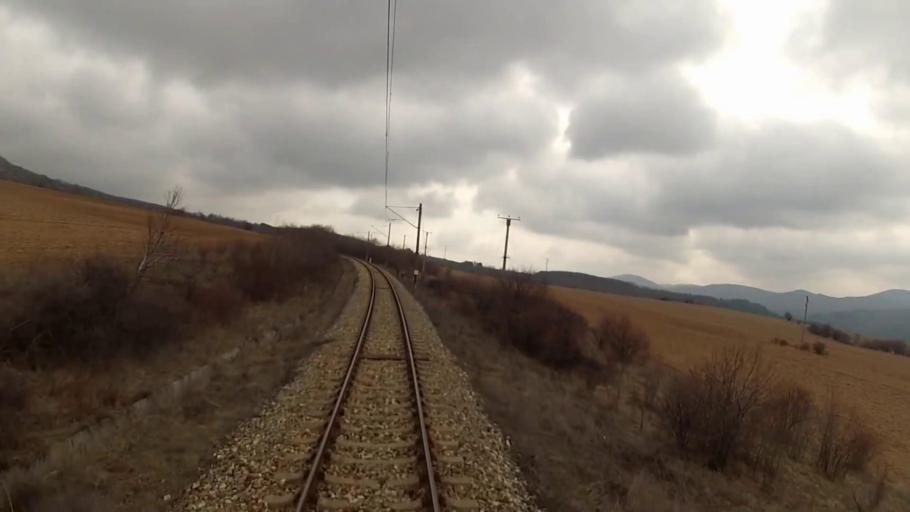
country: BG
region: Sofiya
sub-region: Obshtina Mirkovo
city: Mirkovo
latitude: 42.7070
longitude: 23.9513
